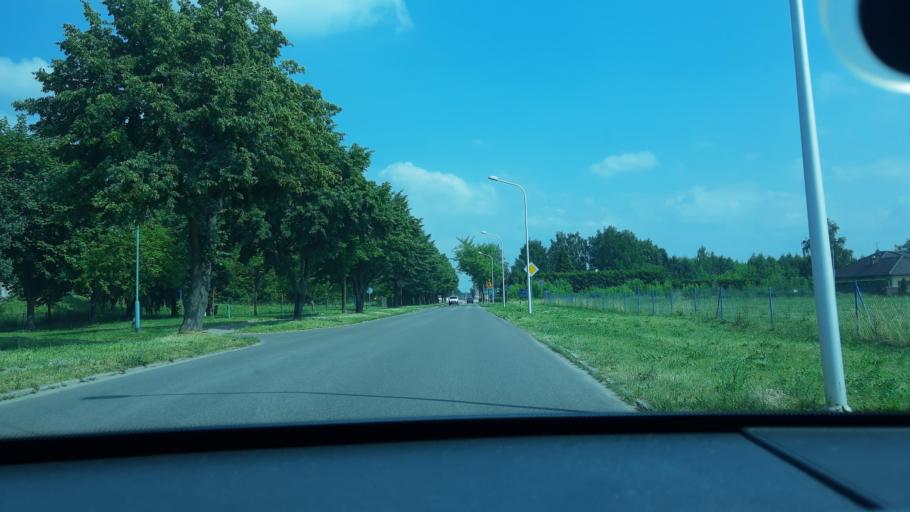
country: PL
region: Lodz Voivodeship
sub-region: Powiat sieradzki
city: Sieradz
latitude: 51.5809
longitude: 18.7104
